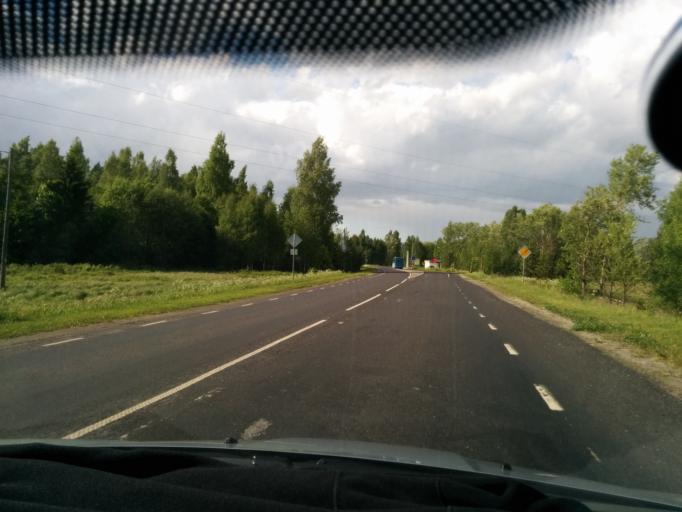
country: EE
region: Harju
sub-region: Loksa linn
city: Loksa
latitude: 59.5674
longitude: 25.7258
